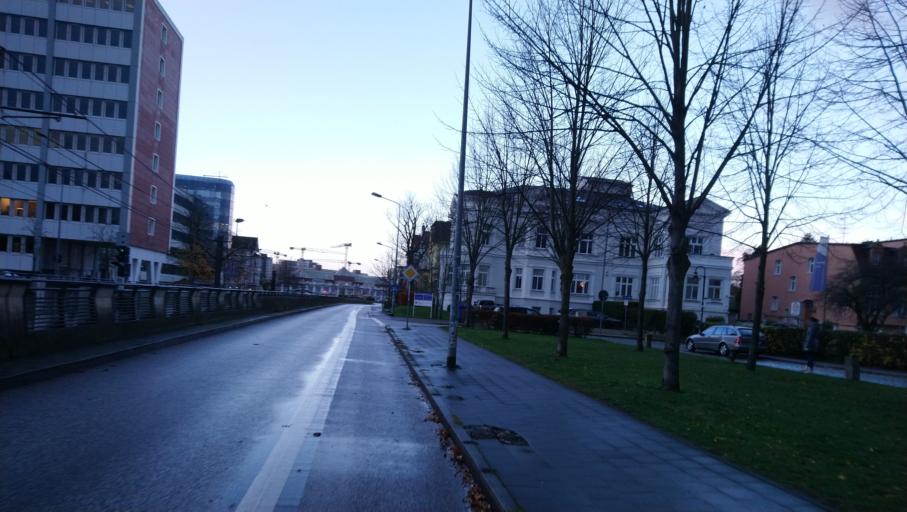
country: DE
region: Mecklenburg-Vorpommern
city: Rostock
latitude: 54.0780
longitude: 12.1393
